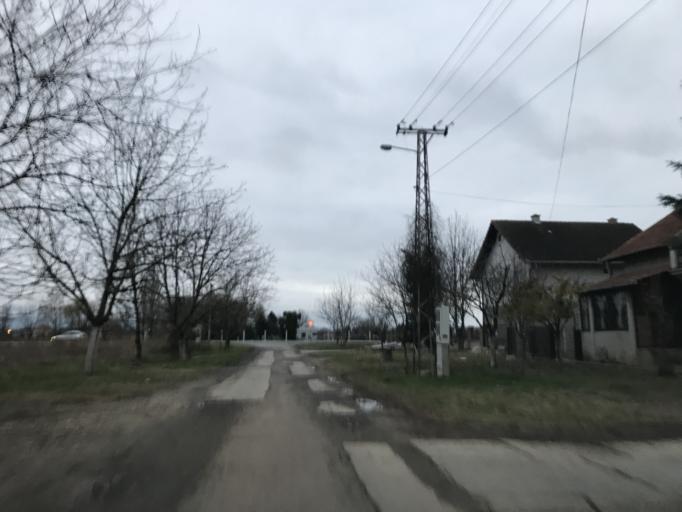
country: RS
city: Rumenka
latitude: 45.2962
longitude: 19.7338
